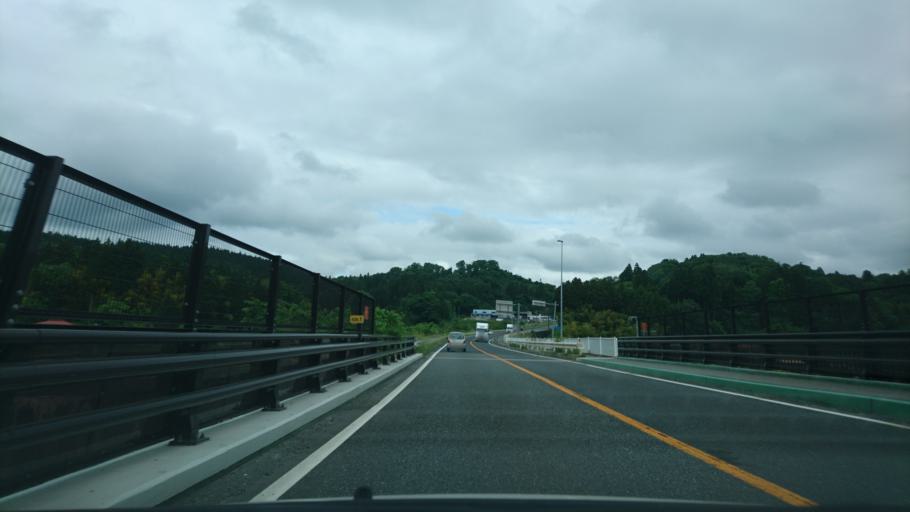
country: JP
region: Iwate
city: Ichinoseki
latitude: 38.8888
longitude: 141.1175
